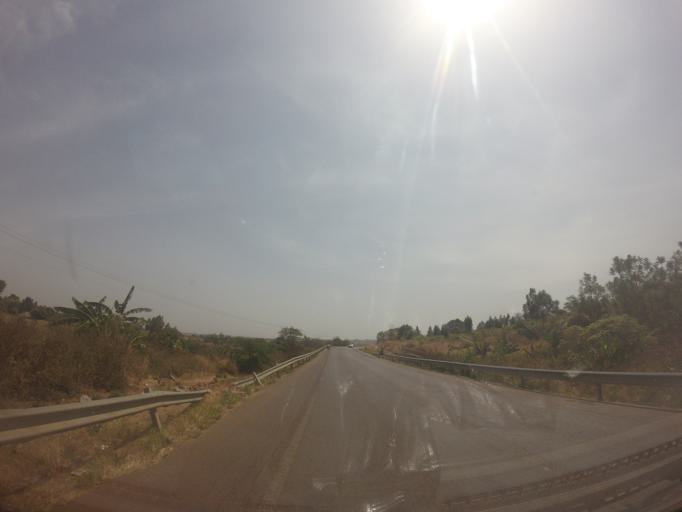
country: UG
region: Northern Region
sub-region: Arua District
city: Arua
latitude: 2.9494
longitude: 30.9365
